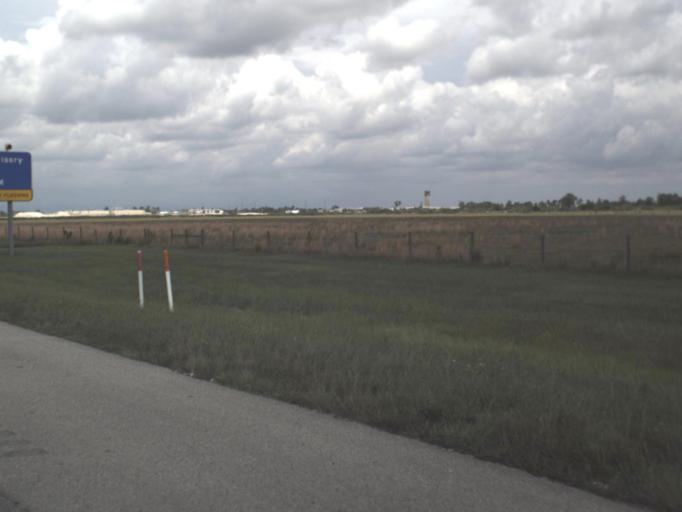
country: US
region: Florida
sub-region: Charlotte County
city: Punta Gorda
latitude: 26.9041
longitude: -82.0083
